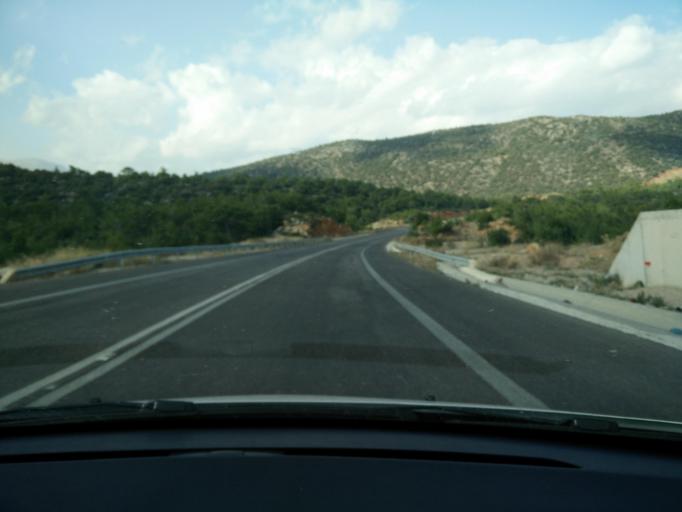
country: GR
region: Crete
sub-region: Nomos Lasithiou
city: Agios Nikolaos
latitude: 35.1406
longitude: 25.7086
